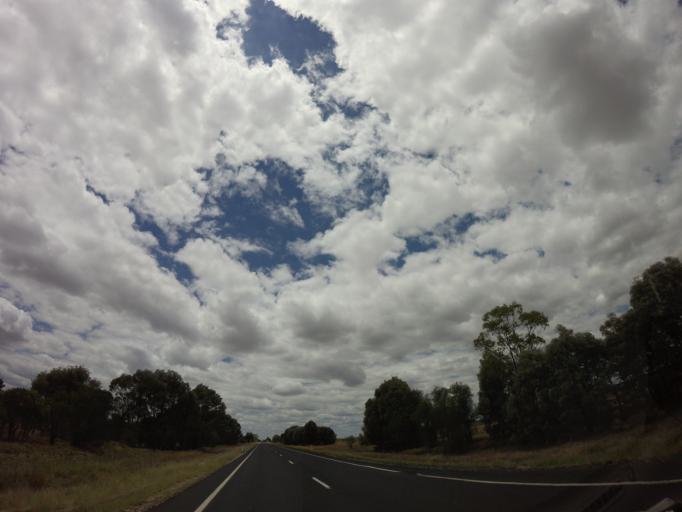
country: AU
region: Queensland
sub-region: Goondiwindi
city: Goondiwindi
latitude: -28.1748
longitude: 150.4868
